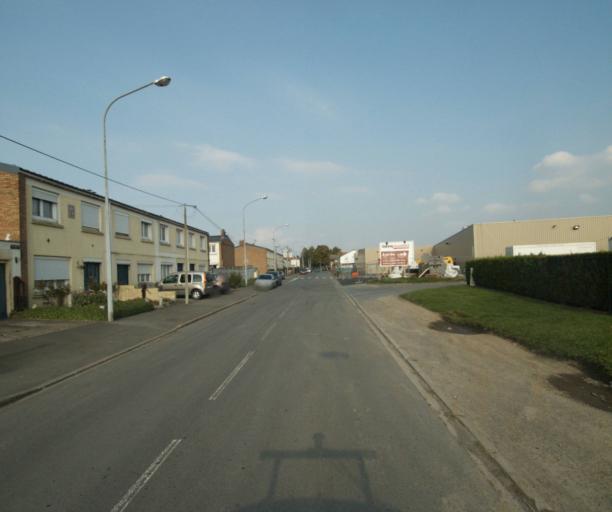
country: FR
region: Nord-Pas-de-Calais
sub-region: Departement du Nord
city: Emmerin
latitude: 50.5983
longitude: 2.9941
